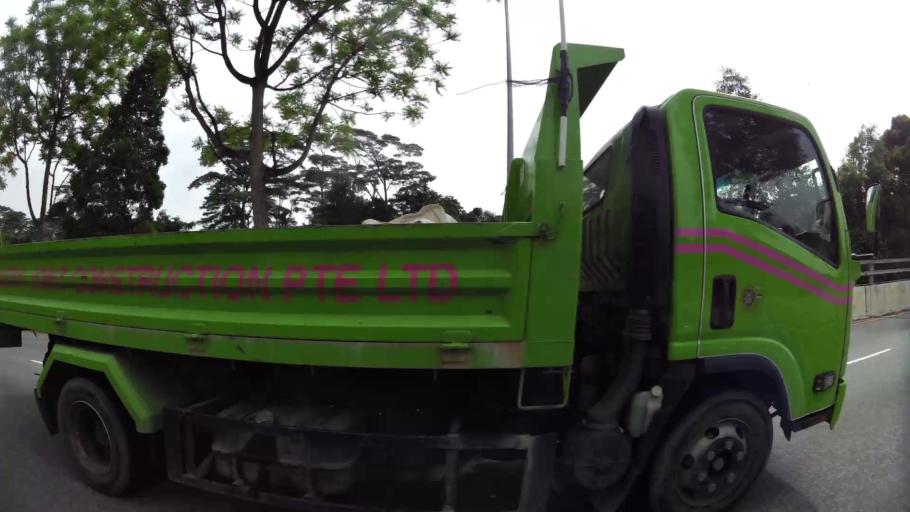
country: MY
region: Johor
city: Johor Bahru
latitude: 1.4164
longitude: 103.7630
